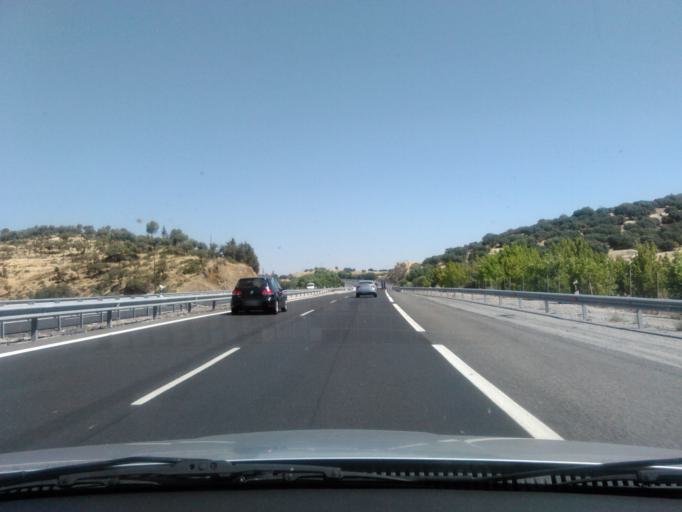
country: ES
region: Castille-La Mancha
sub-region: Provincia de Ciudad Real
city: Viso del Marques
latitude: 38.4458
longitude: -3.4971
